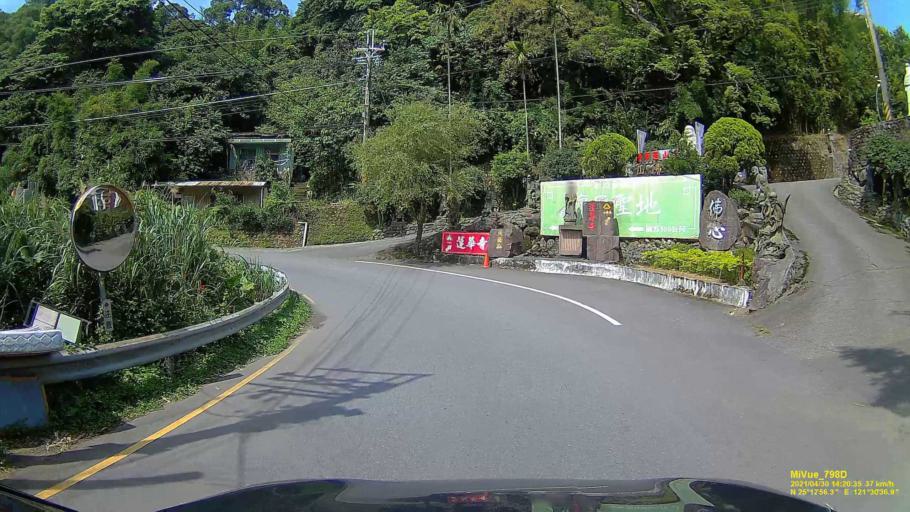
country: TW
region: Taipei
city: Taipei
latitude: 25.2157
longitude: 121.5103
